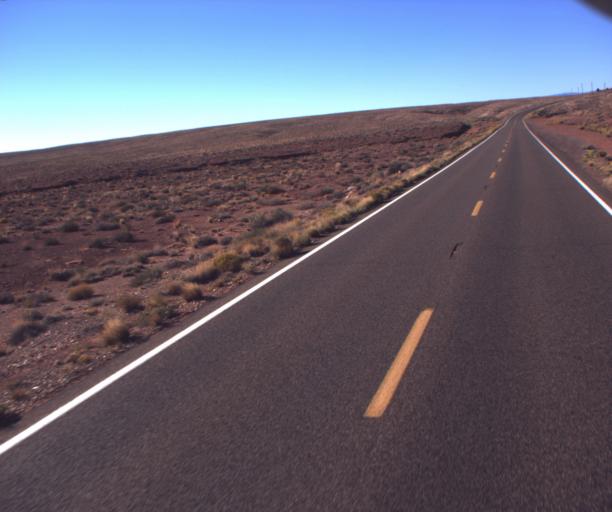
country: US
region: Arizona
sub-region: Coconino County
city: Page
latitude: 36.7703
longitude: -111.7014
